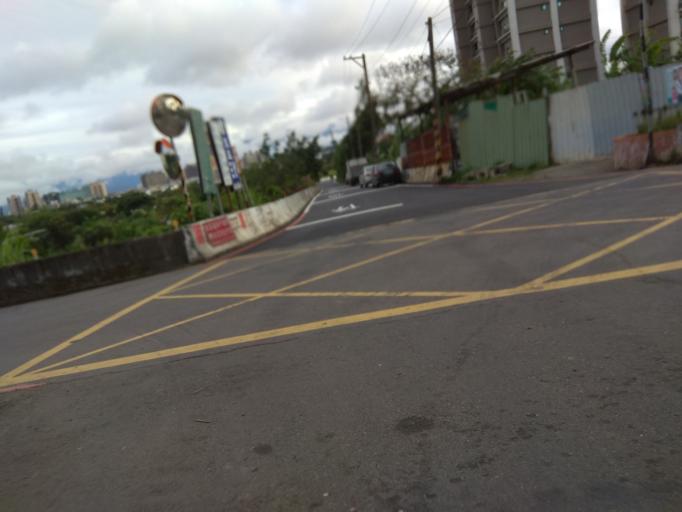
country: TW
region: Taiwan
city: Daxi
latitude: 24.9274
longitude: 121.1964
